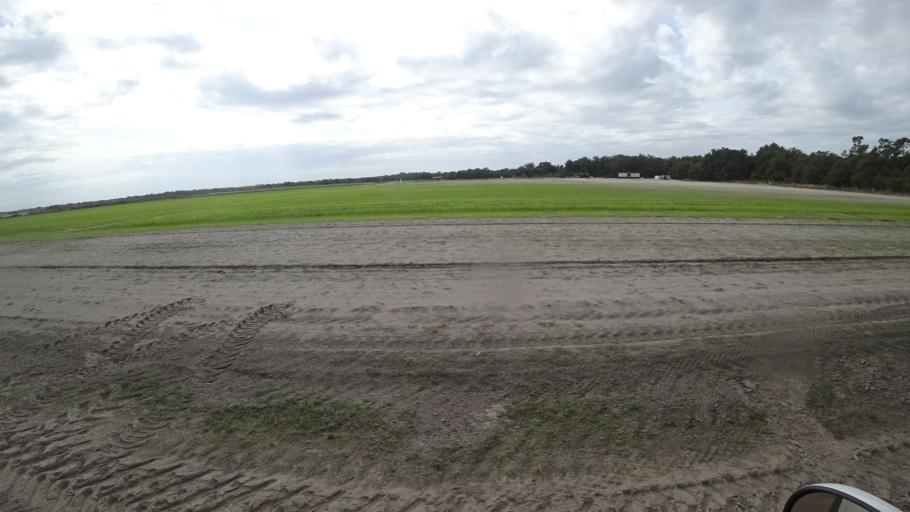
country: US
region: Florida
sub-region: Hillsborough County
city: Wimauma
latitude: 27.5679
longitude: -82.3112
